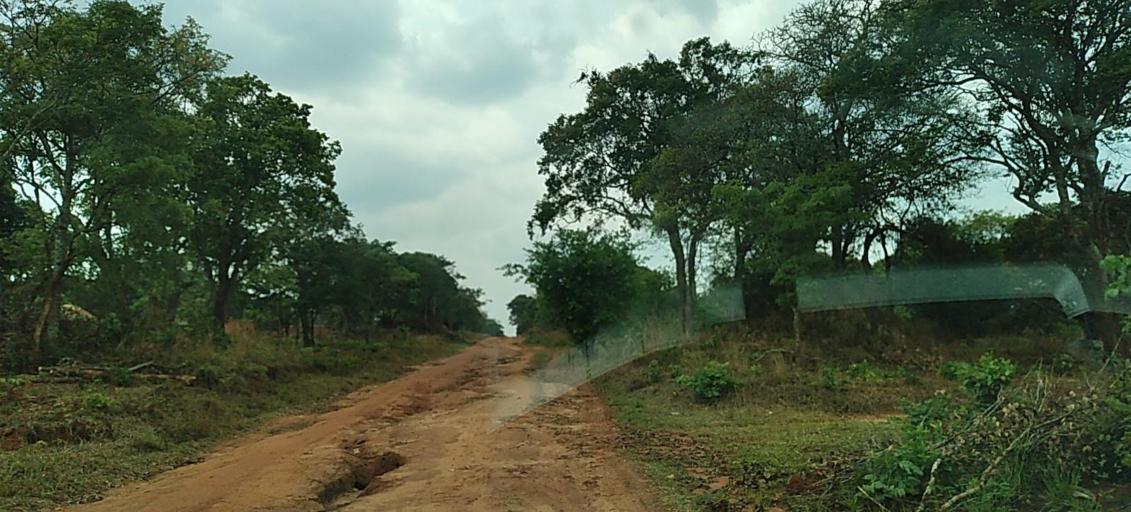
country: ZM
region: North-Western
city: Mwinilunga
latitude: -11.5347
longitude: 24.7837
